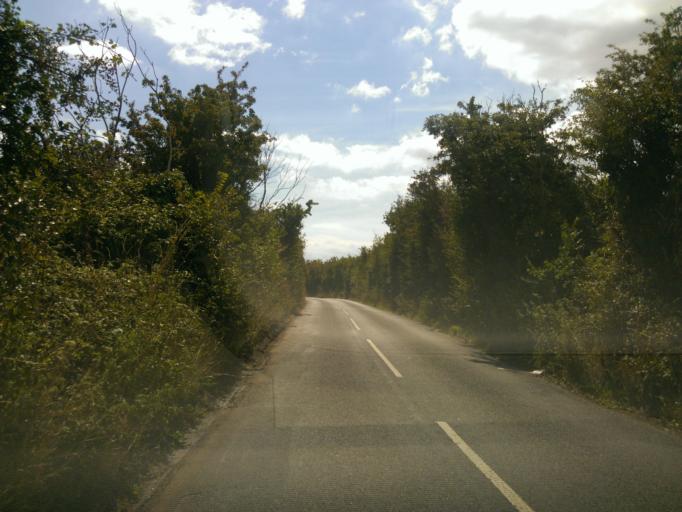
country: GB
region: England
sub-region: Essex
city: Saint Osyth
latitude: 51.7888
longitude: 1.0869
